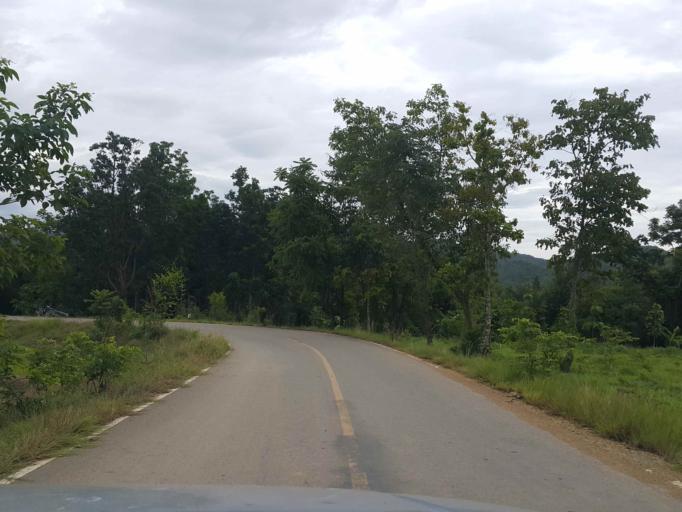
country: TH
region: Sukhothai
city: Thung Saliam
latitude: 17.3317
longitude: 99.4400
